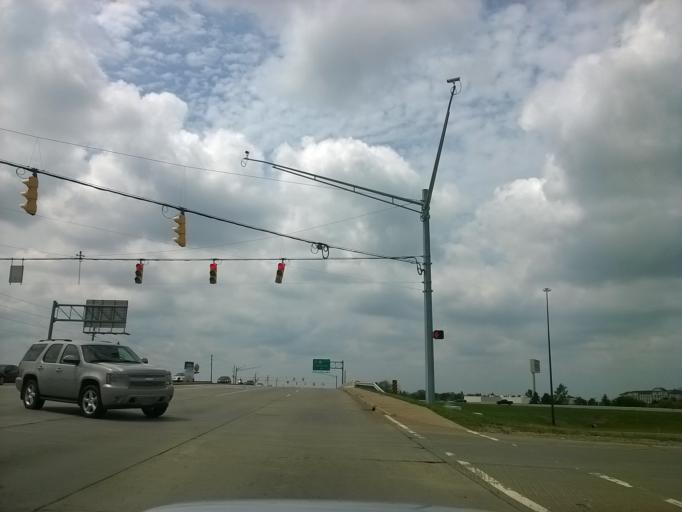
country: US
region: Indiana
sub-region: Hamilton County
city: Fishers
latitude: 39.9273
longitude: -86.0281
